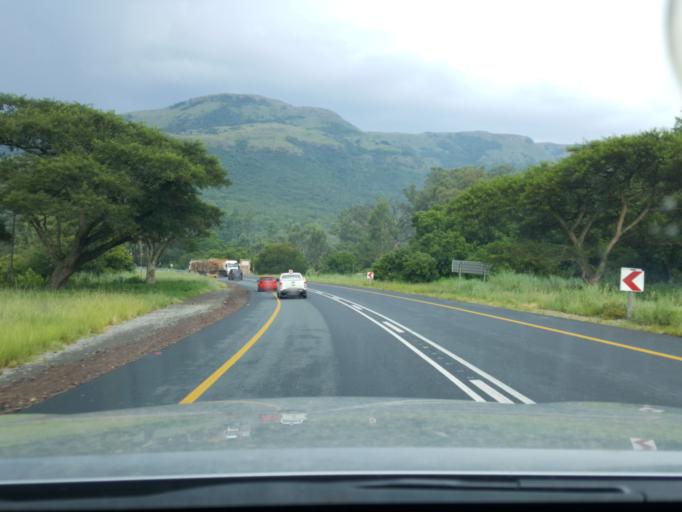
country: ZA
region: Mpumalanga
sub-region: Nkangala District Municipality
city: Belfast
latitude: -25.6469
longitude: 30.3905
